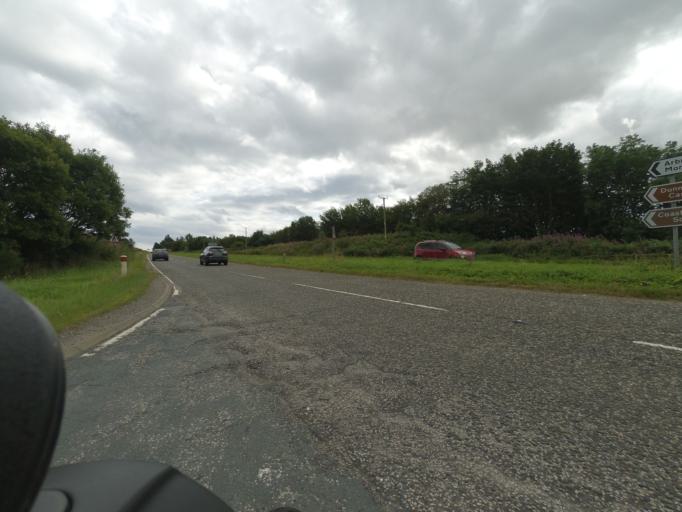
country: GB
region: Scotland
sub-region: Aberdeenshire
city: Stonehaven
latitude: 56.9497
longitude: -2.2257
